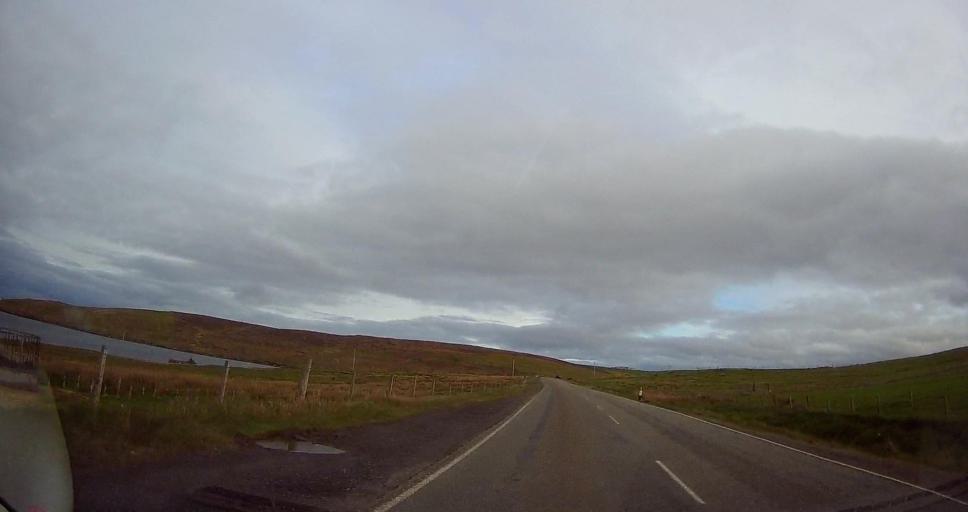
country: GB
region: Scotland
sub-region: Shetland Islands
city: Lerwick
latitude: 60.4650
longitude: -1.2127
